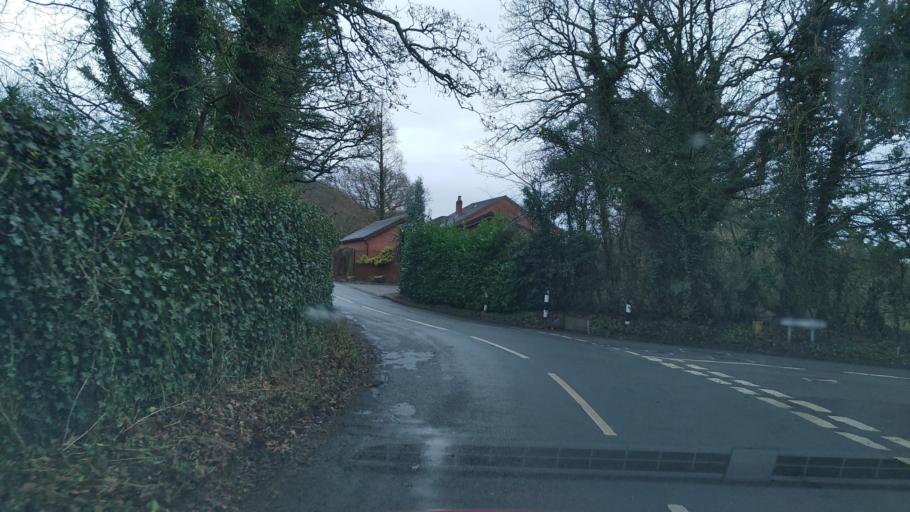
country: GB
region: England
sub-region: Lancashire
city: Clayton-le-Woods
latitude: 53.7073
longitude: -2.6644
